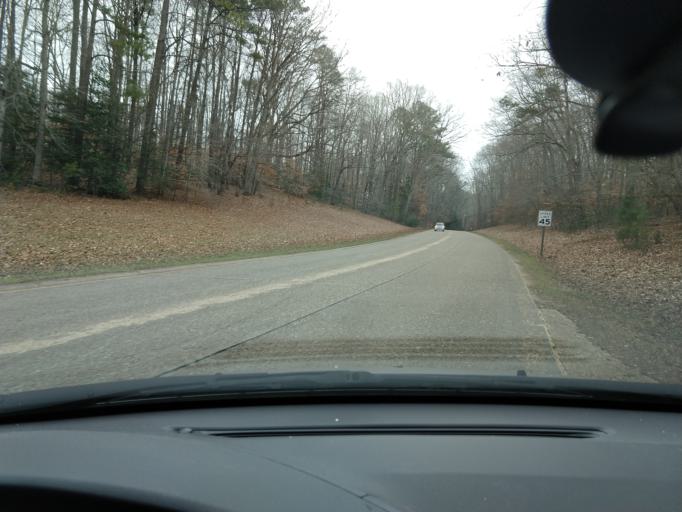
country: US
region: Virginia
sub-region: City of Williamsburg
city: Williamsburg
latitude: 37.2830
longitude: -76.6407
